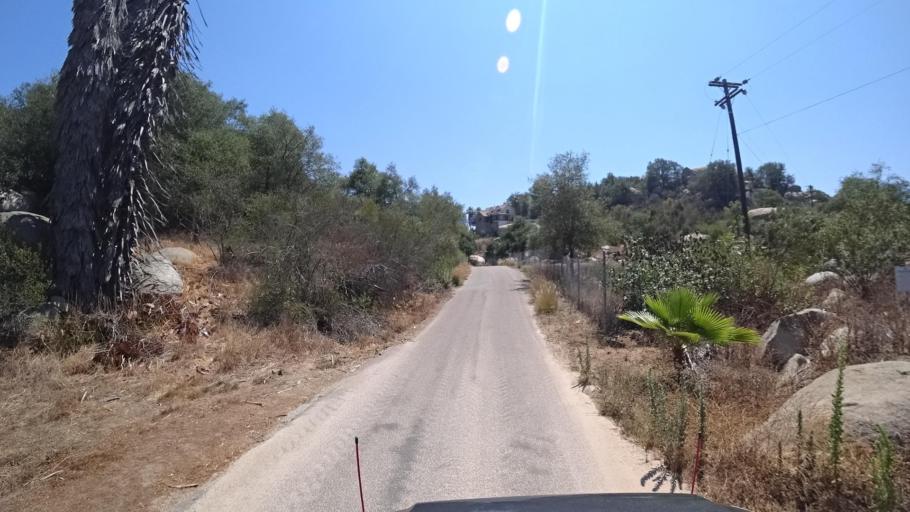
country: US
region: California
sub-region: San Diego County
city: Fallbrook
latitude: 33.4365
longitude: -117.2804
